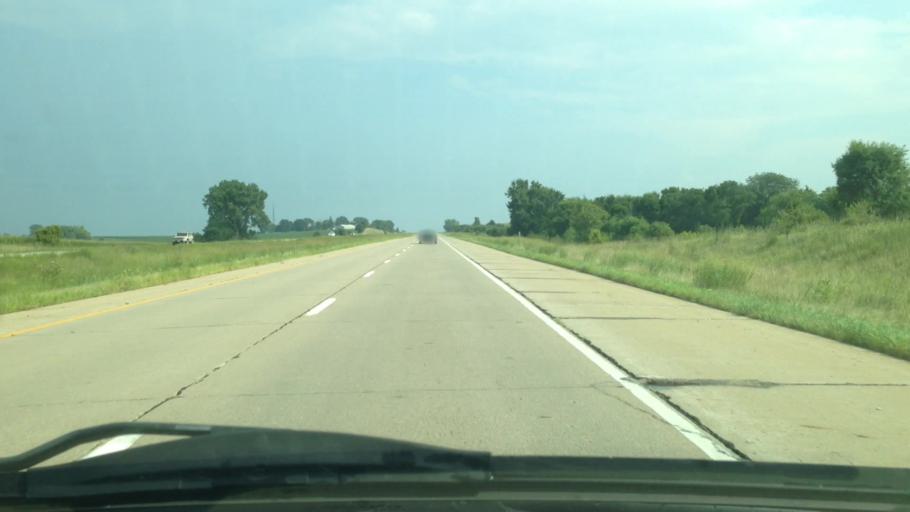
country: US
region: Iowa
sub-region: Benton County
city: Urbana
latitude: 42.2971
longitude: -91.9597
